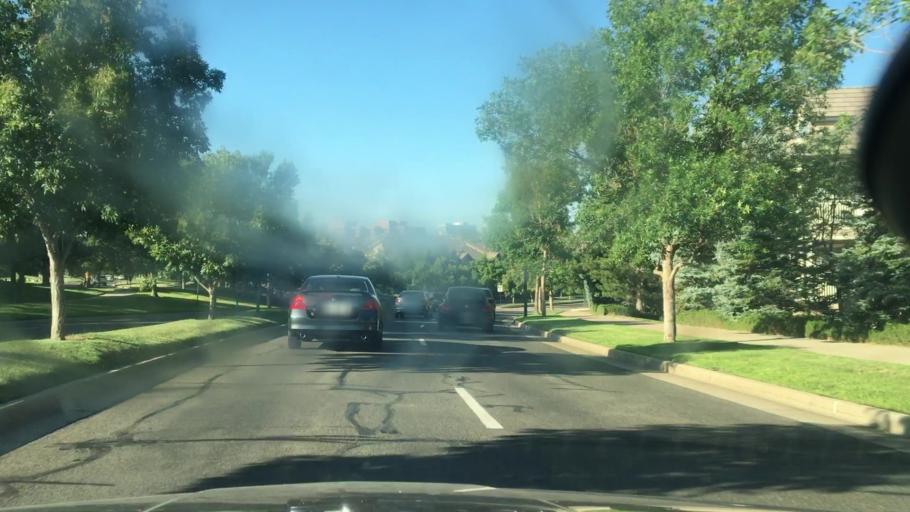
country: US
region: Colorado
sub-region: Arapahoe County
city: Castlewood
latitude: 39.6217
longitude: -104.8855
